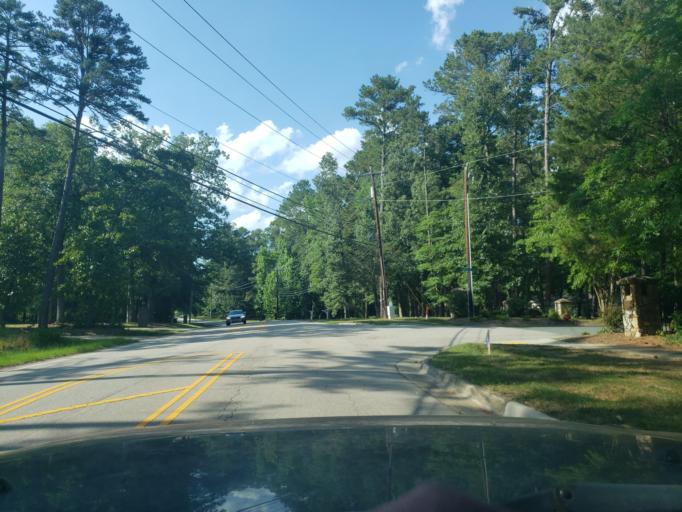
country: US
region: North Carolina
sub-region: Durham County
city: Durham
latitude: 35.9828
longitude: -78.9899
